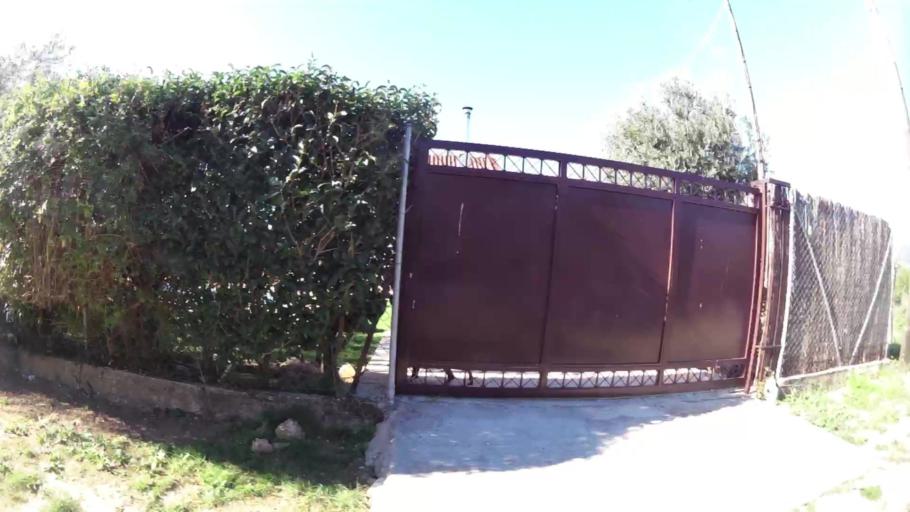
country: GR
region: Attica
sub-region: Nomarchia Anatolikis Attikis
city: Varybobi
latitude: 38.1214
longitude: 23.7850
